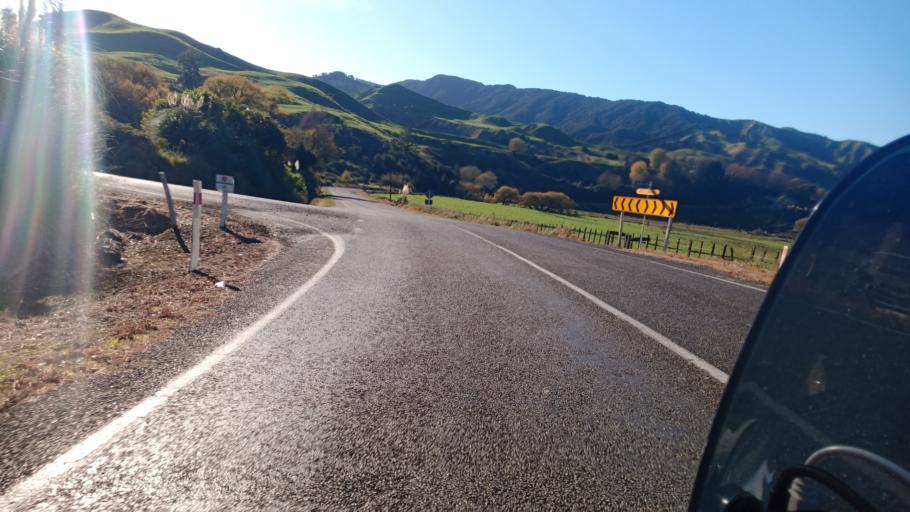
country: NZ
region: Hawke's Bay
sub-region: Wairoa District
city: Wairoa
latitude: -38.8788
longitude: 177.2369
